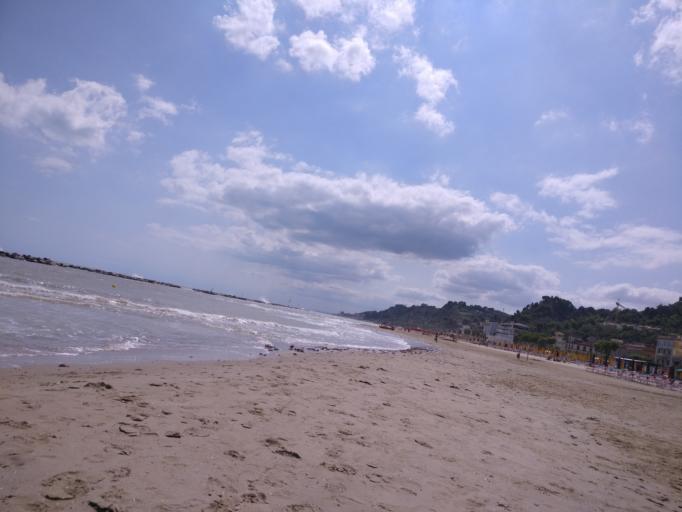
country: IT
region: The Marches
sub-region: Provincia di Ascoli Piceno
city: Cupra Marittima
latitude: 43.0261
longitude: 13.8617
